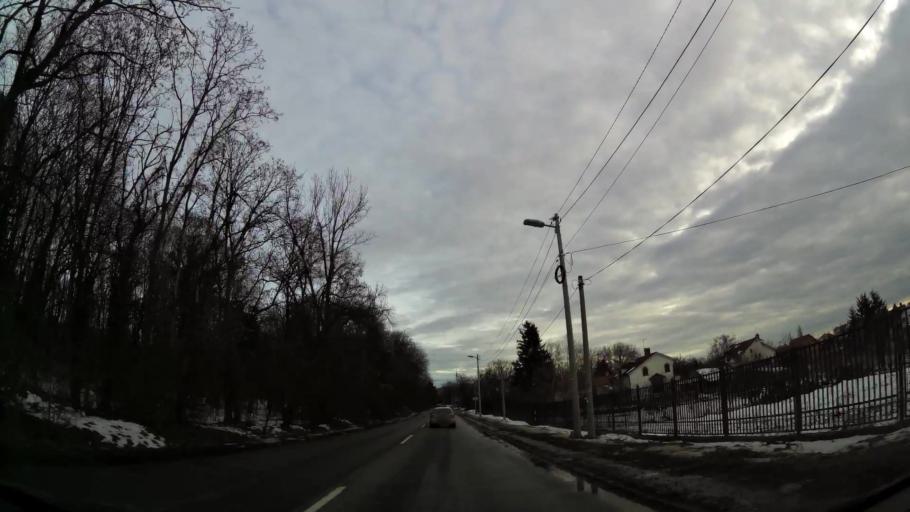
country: RS
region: Central Serbia
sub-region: Belgrade
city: Rakovica
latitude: 44.7283
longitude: 20.4855
